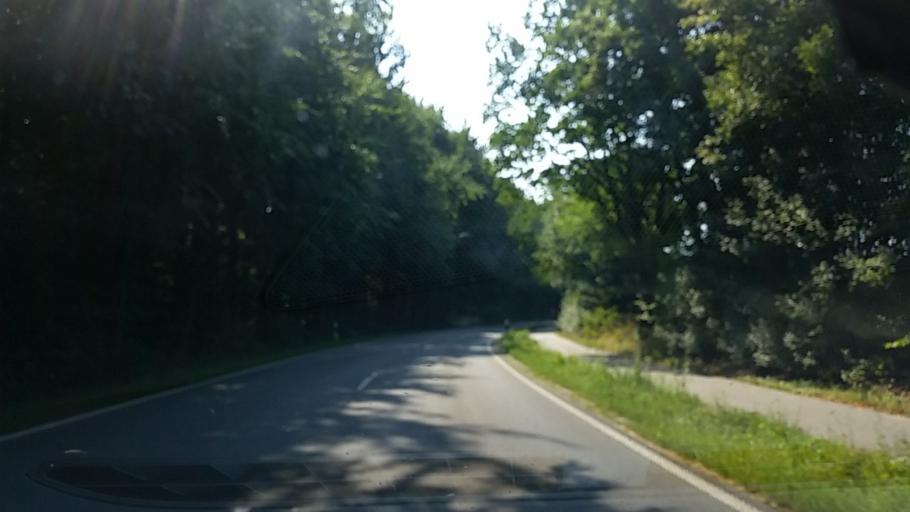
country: DE
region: Schleswig-Holstein
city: Grande
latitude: 53.5742
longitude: 10.3669
